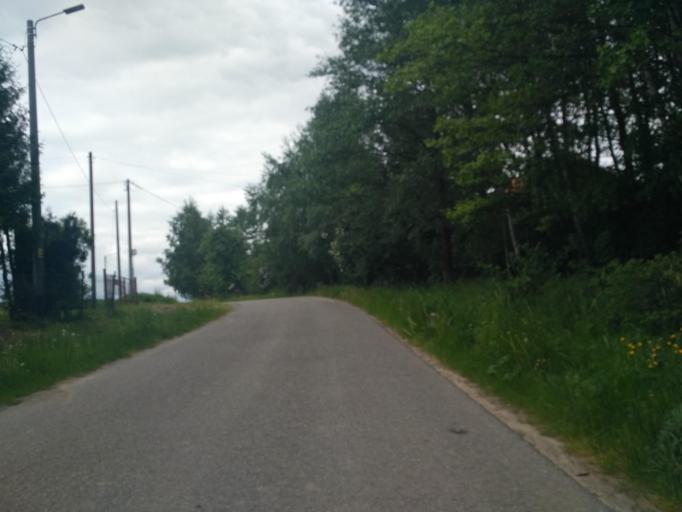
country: PL
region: Subcarpathian Voivodeship
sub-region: Powiat jasielski
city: Tarnowiec
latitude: 49.6948
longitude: 21.5811
